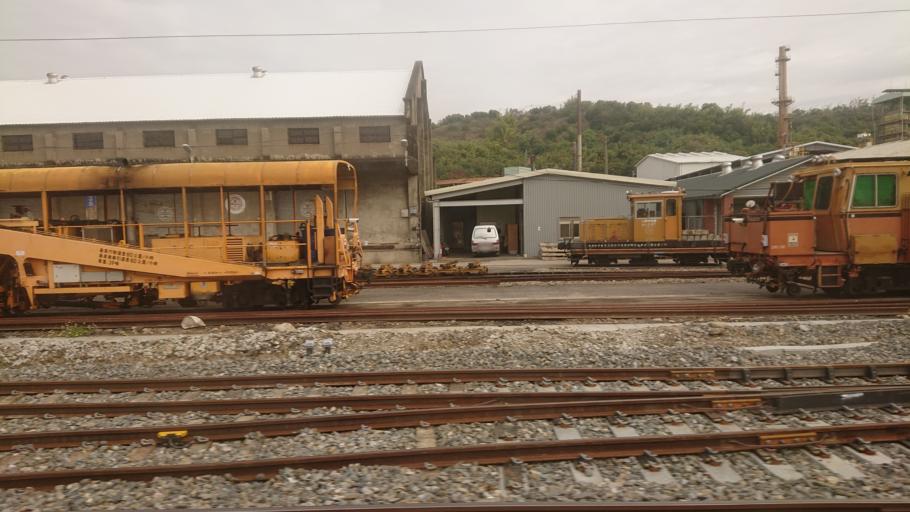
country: TW
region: Taiwan
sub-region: Changhua
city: Chang-hua
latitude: 24.1152
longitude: 120.5887
